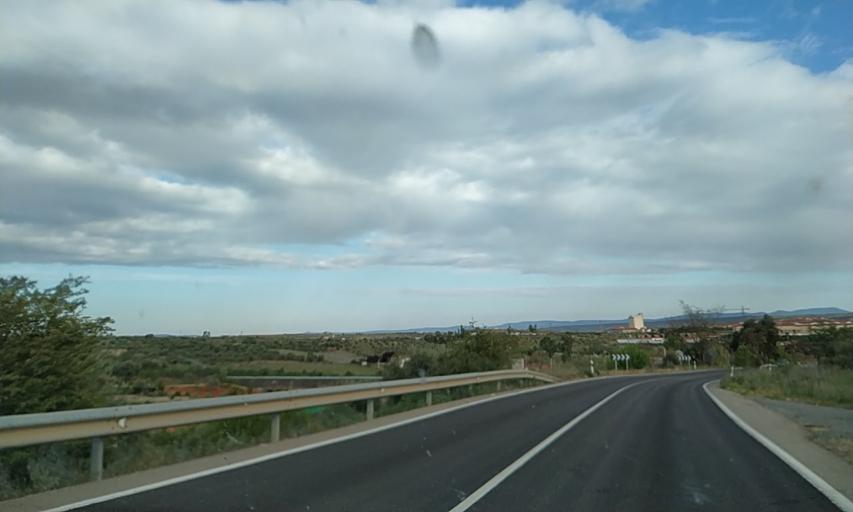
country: ES
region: Extremadura
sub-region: Provincia de Caceres
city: Coria
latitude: 39.9992
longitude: -6.5486
